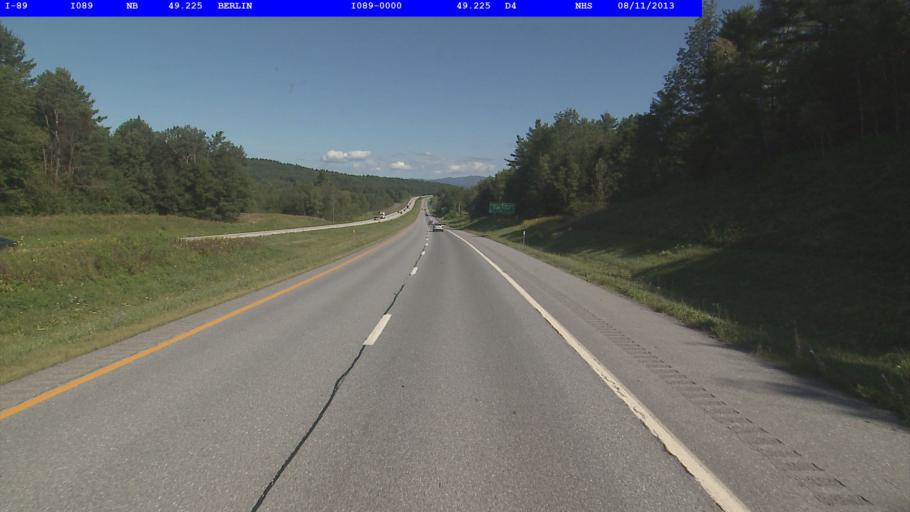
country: US
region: Vermont
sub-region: Washington County
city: Montpelier
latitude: 44.2008
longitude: -72.5776
